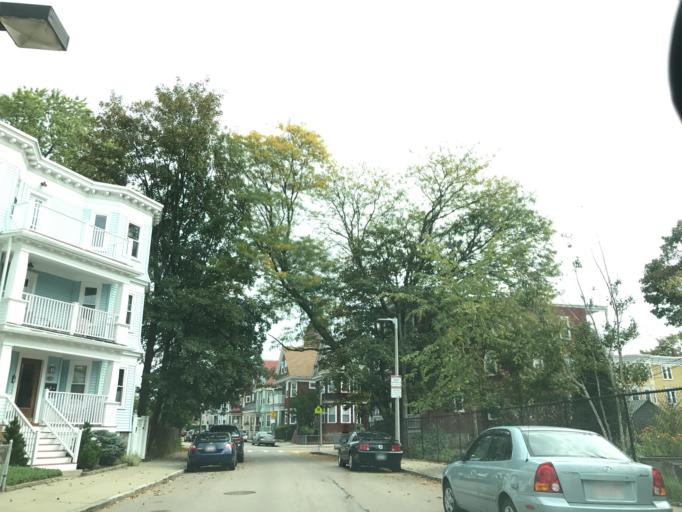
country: US
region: Massachusetts
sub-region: Suffolk County
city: South Boston
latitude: 42.3208
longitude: -71.0596
